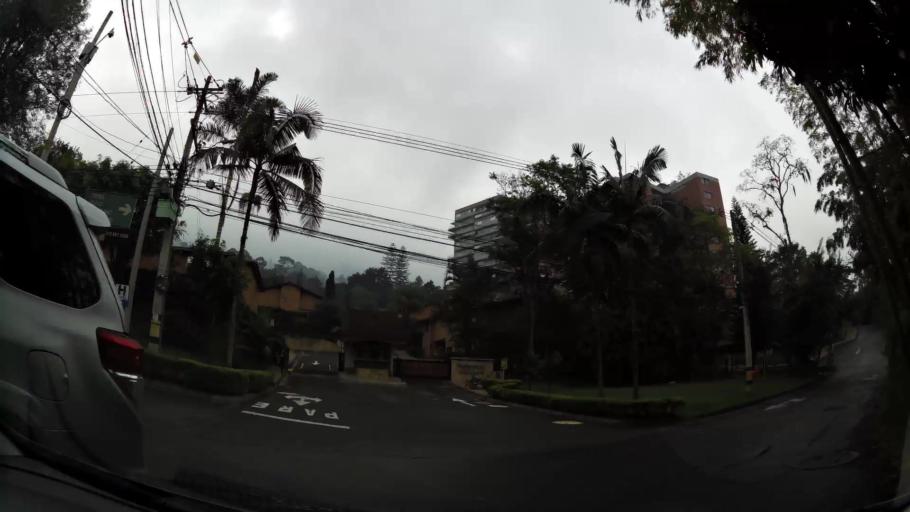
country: CO
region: Antioquia
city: Envigado
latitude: 6.1778
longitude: -75.5611
